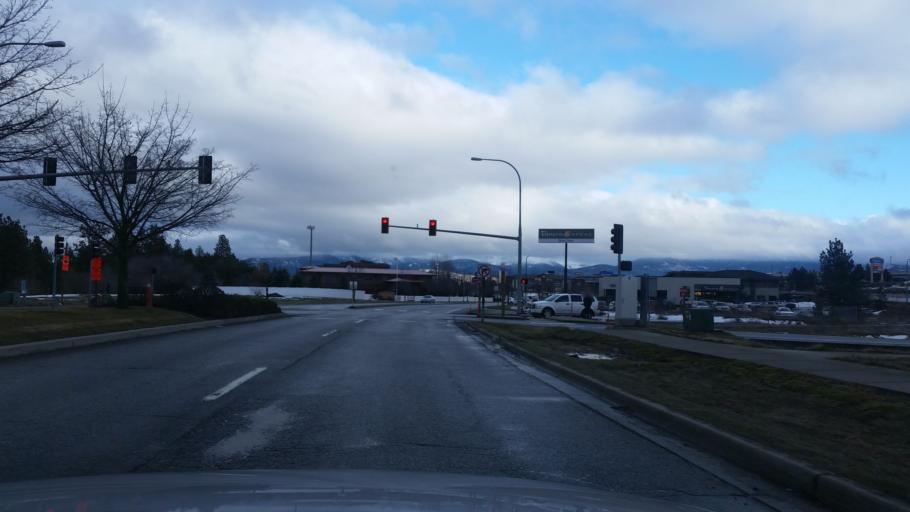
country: US
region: Washington
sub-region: Spokane County
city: Veradale
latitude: 47.6707
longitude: -117.1949
